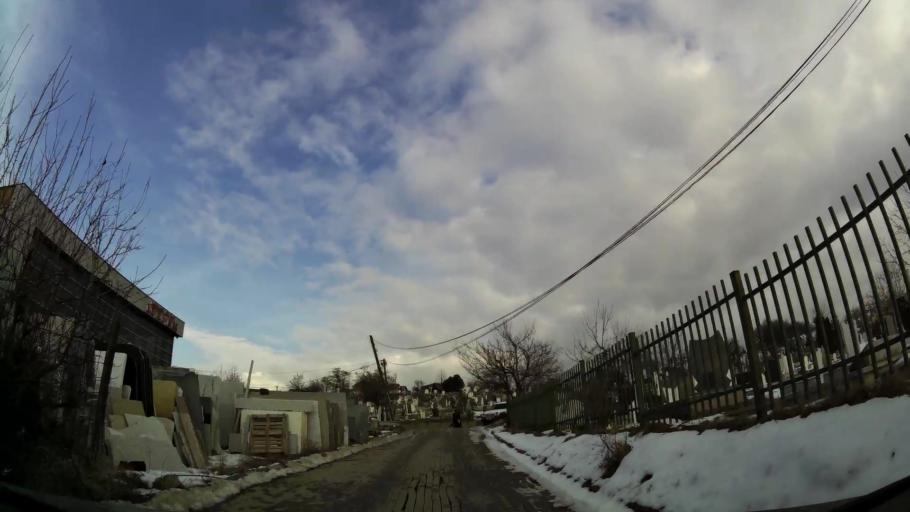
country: XK
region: Pristina
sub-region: Komuna e Prishtines
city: Pristina
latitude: 42.6728
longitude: 21.1516
